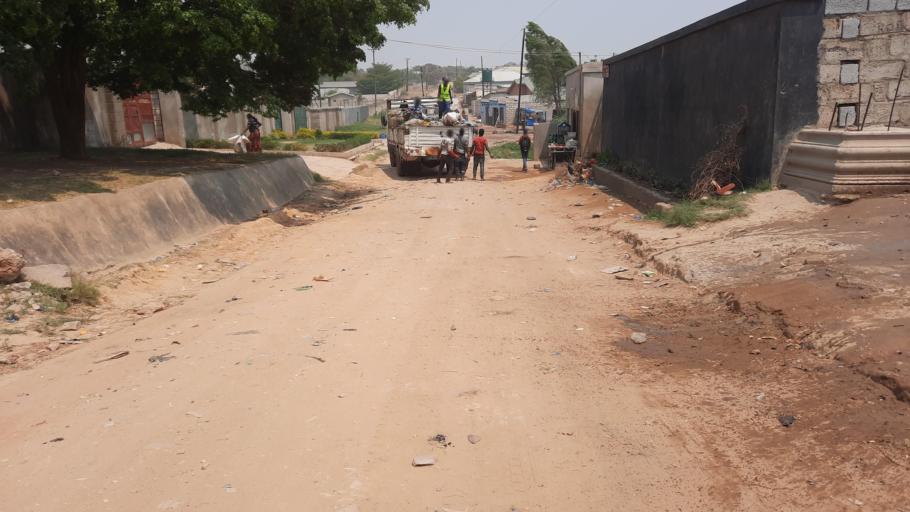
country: ZM
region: Lusaka
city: Lusaka
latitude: -15.4100
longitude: 28.3768
